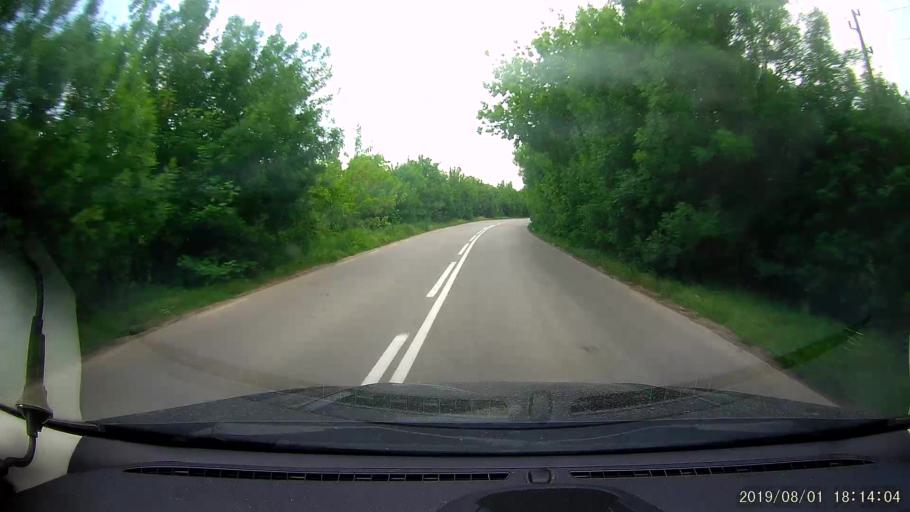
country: BG
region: Silistra
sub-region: Obshtina Dulovo
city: Dulovo
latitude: 43.7764
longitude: 27.1293
